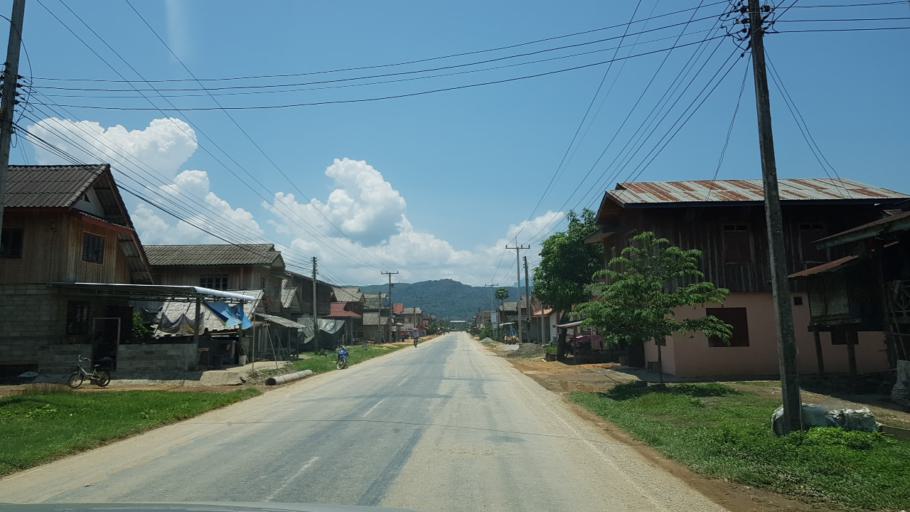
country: LA
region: Vientiane
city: Muang Kasi
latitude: 19.2490
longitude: 102.2479
